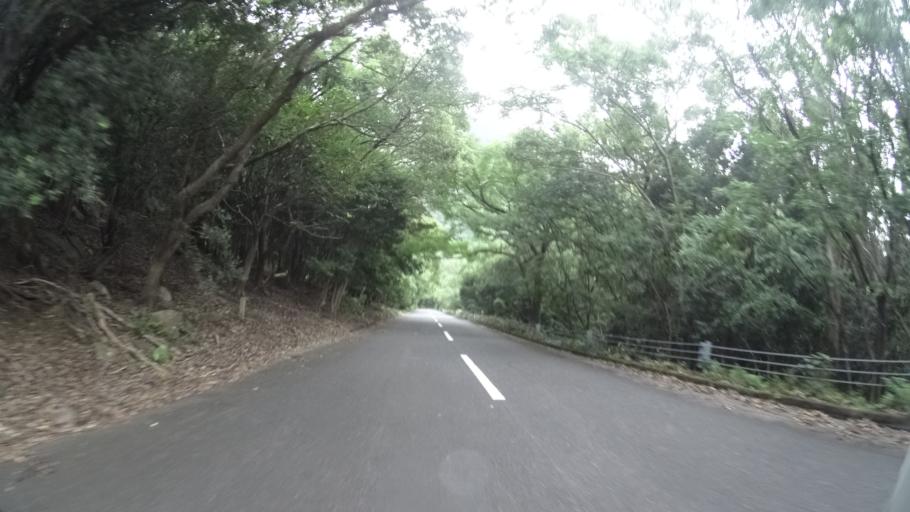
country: JP
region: Kagoshima
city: Nishinoomote
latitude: 30.3188
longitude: 130.3994
